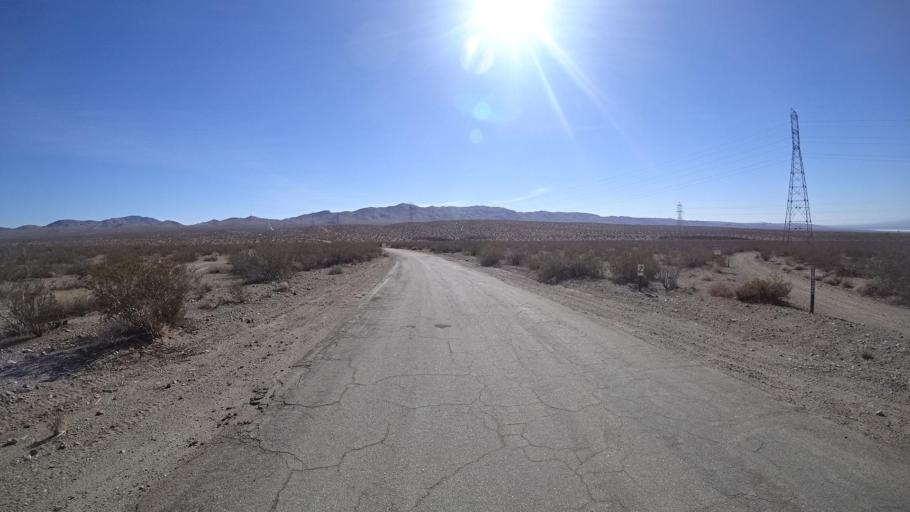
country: US
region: California
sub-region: Kern County
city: Ridgecrest
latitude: 35.4217
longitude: -117.6930
